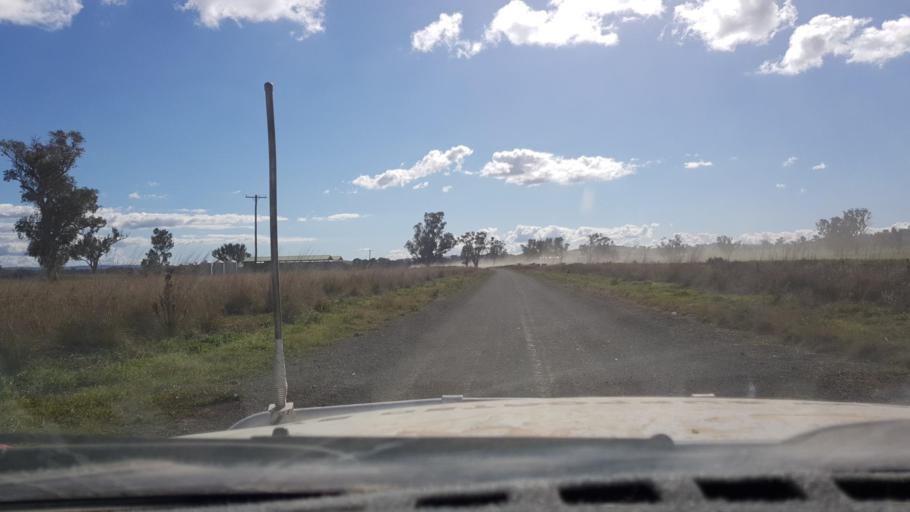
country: AU
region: New South Wales
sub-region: Narrabri
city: Blair Athol
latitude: -30.5322
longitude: 150.4421
